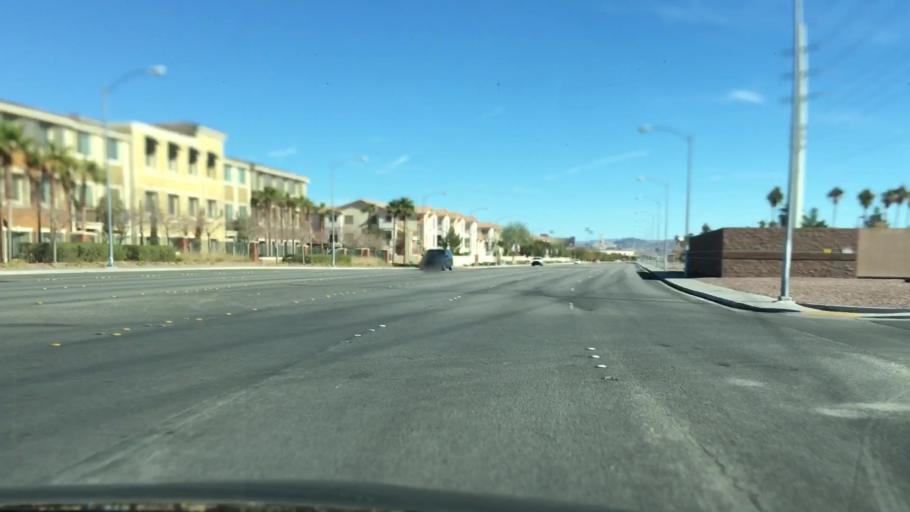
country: US
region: Nevada
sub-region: Clark County
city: Whitney
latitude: 36.0855
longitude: -115.0303
